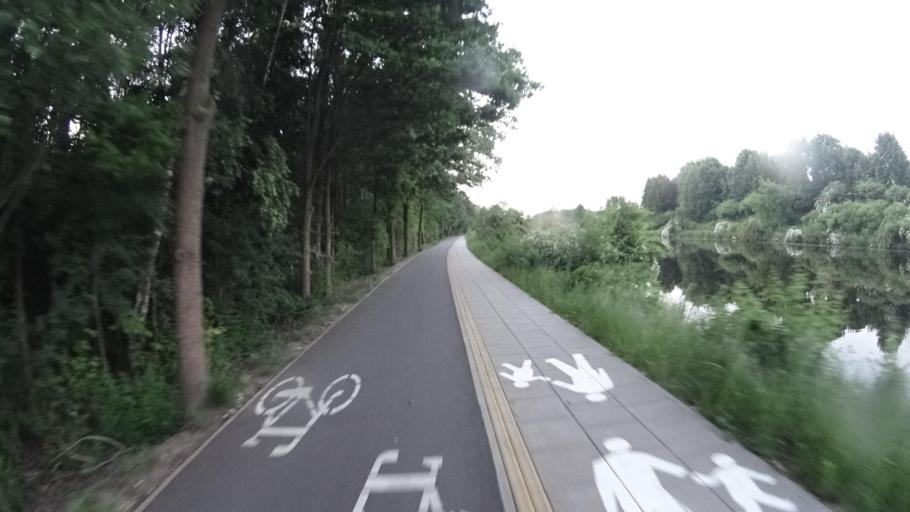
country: PL
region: Masovian Voivodeship
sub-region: Powiat legionowski
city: Stanislawow Pierwszy
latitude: 52.3900
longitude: 21.0373
